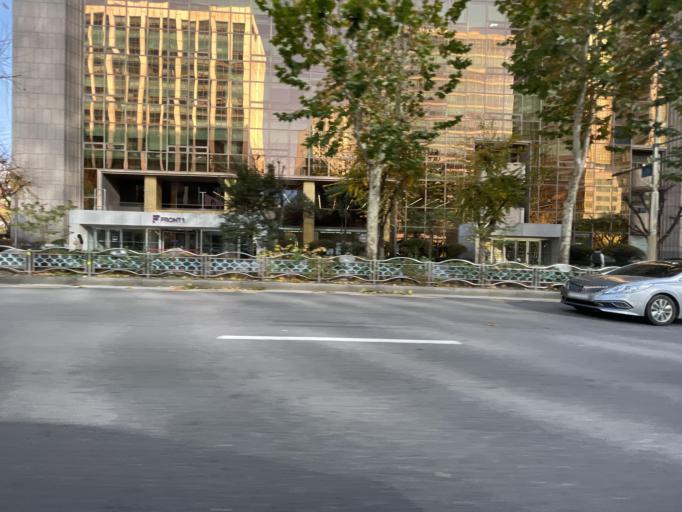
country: KR
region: Seoul
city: Seoul
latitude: 37.5456
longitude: 126.9523
